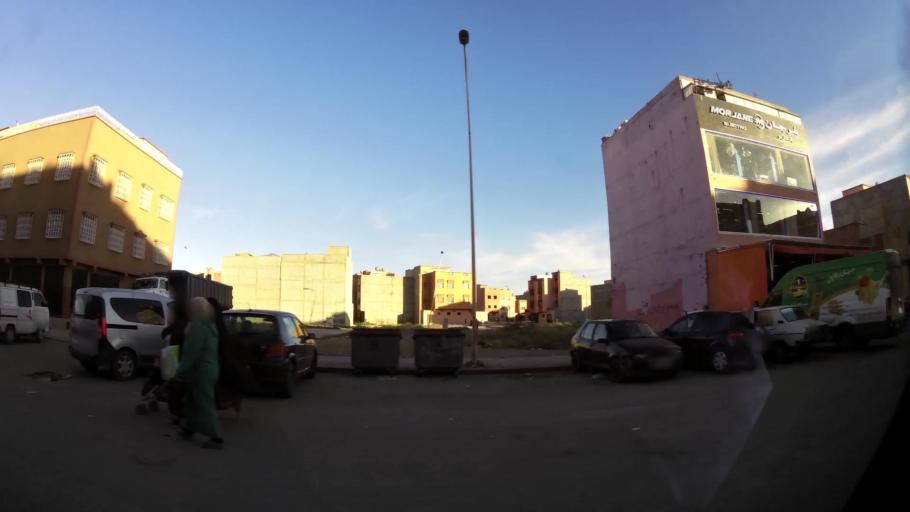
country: MA
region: Marrakech-Tensift-Al Haouz
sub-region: Marrakech
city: Marrakesh
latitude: 31.7484
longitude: -8.1184
